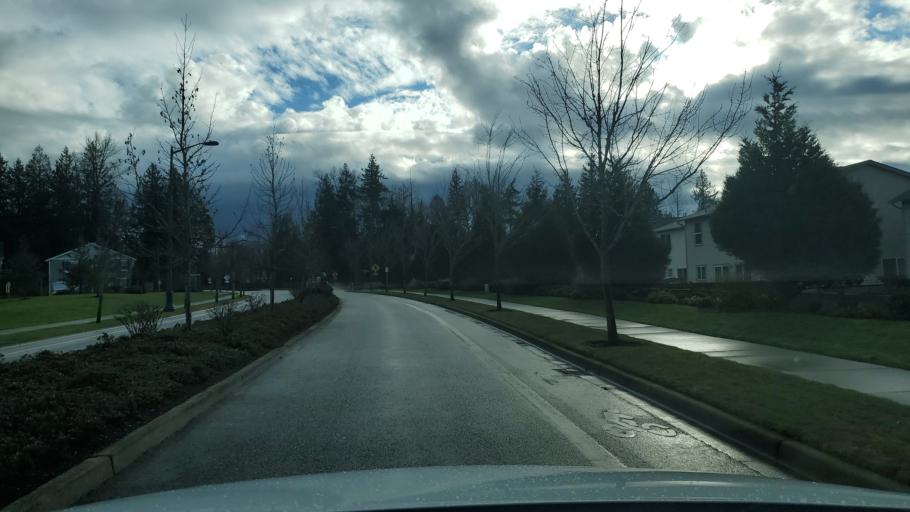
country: US
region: Washington
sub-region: Skagit County
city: Big Lake
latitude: 48.4277
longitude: -122.2778
